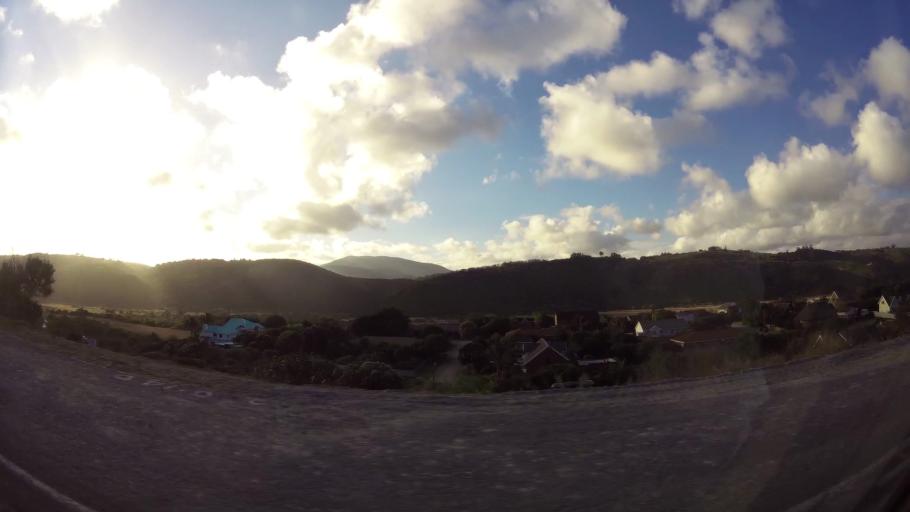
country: ZA
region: Western Cape
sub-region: Eden District Municipality
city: George
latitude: -33.9964
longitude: 22.6117
